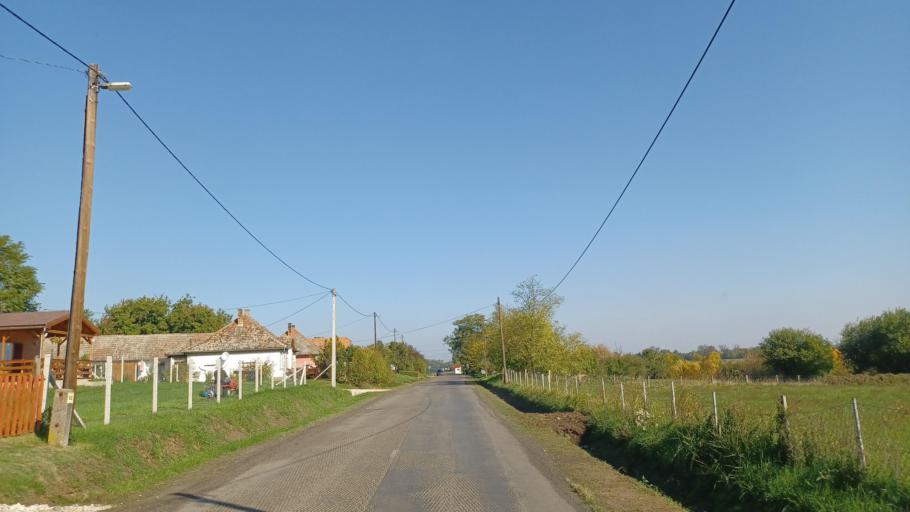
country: HU
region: Tolna
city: Nagydorog
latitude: 46.5592
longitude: 18.5907
